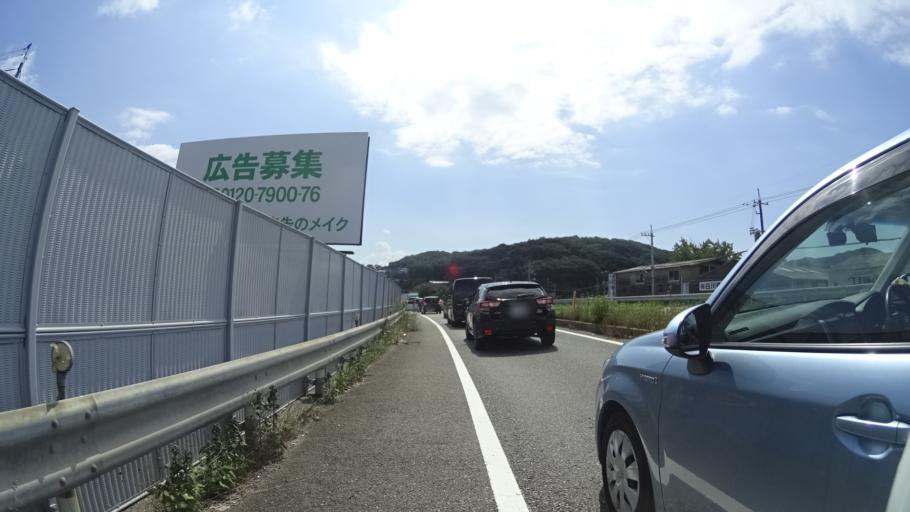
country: JP
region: Yamaguchi
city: Shimonoseki
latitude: 33.9787
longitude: 130.9469
